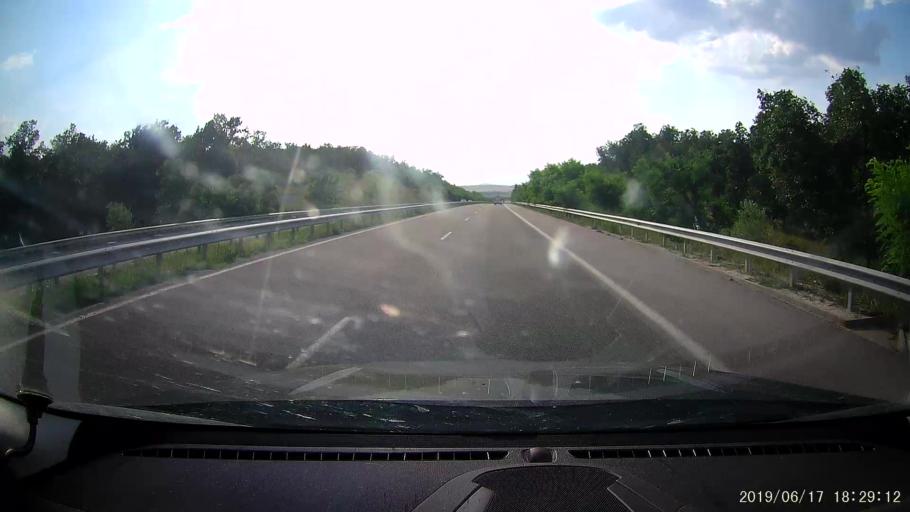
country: BG
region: Khaskovo
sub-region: Obshtina Dimitrovgrad
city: Dimitrovgrad
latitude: 42.0273
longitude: 25.5606
